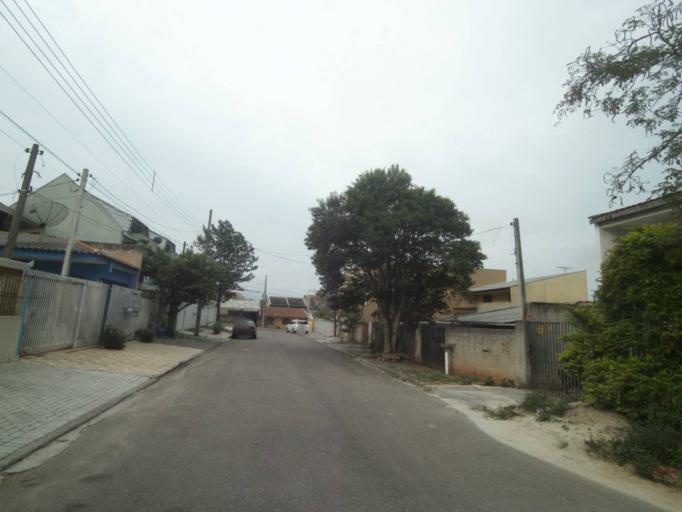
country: BR
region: Parana
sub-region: Sao Jose Dos Pinhais
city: Sao Jose dos Pinhais
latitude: -25.5513
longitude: -49.2648
